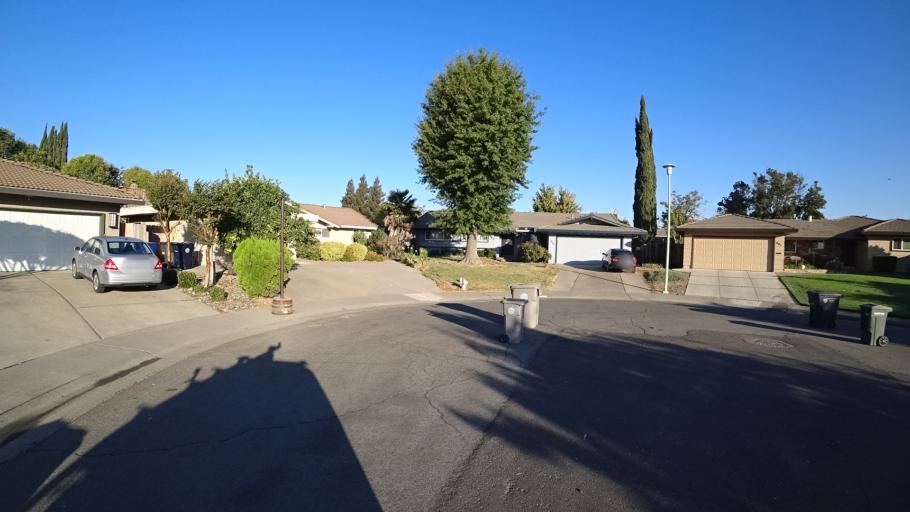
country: US
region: California
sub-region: Yolo County
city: West Sacramento
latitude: 38.5147
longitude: -121.5372
